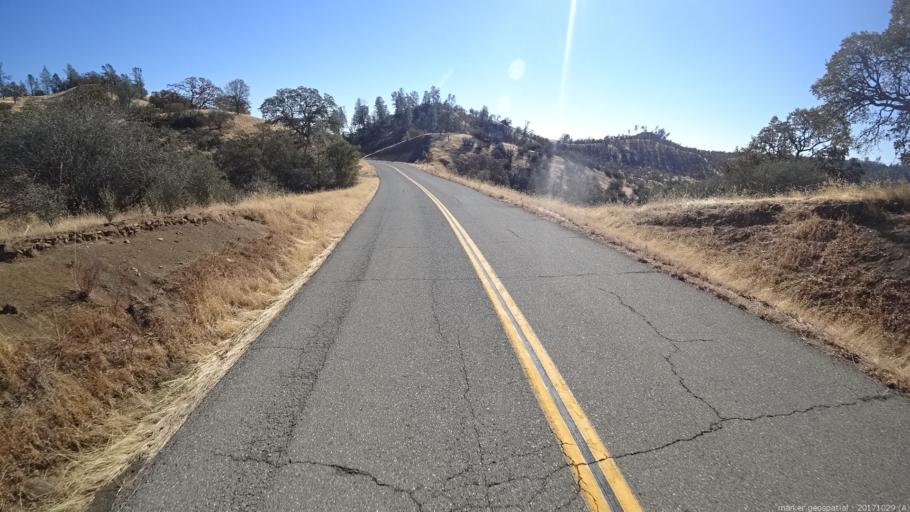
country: US
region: California
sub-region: Shasta County
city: Shasta
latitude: 40.4456
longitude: -122.6832
